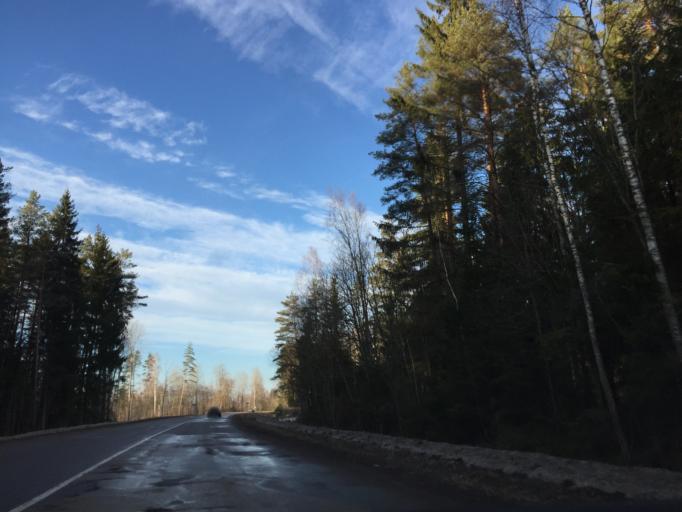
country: LV
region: Kekava
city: Balozi
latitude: 56.7615
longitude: 24.1077
